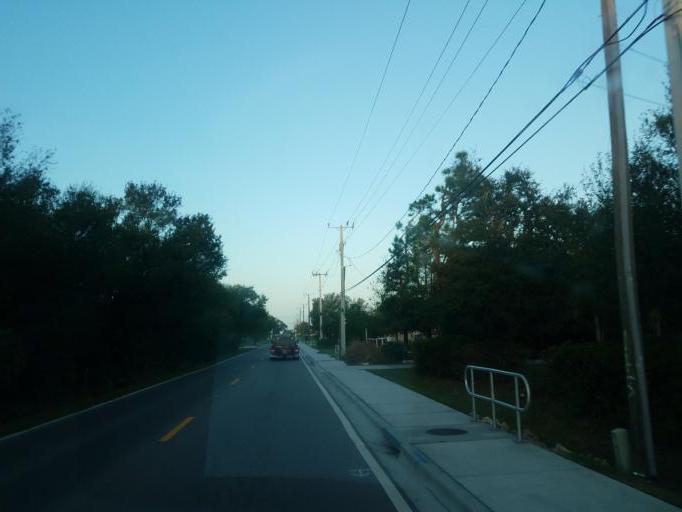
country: US
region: Florida
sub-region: Manatee County
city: Whitfield
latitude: 27.4036
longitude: -82.5397
